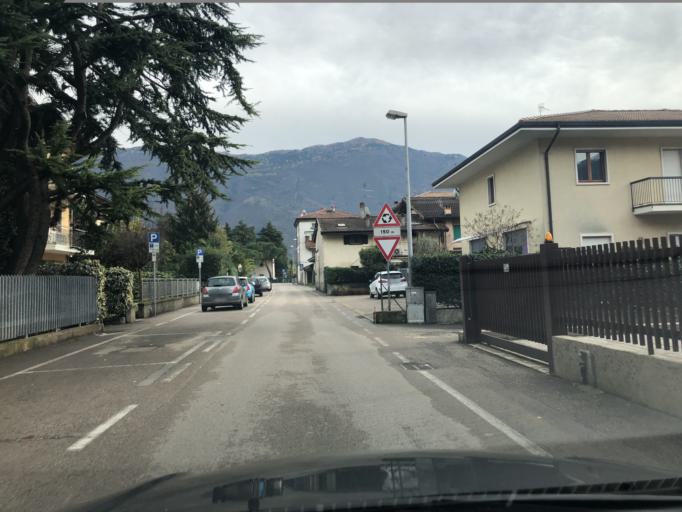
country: IT
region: Trentino-Alto Adige
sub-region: Provincia di Trento
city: Arco
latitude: 45.9161
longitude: 10.8771
